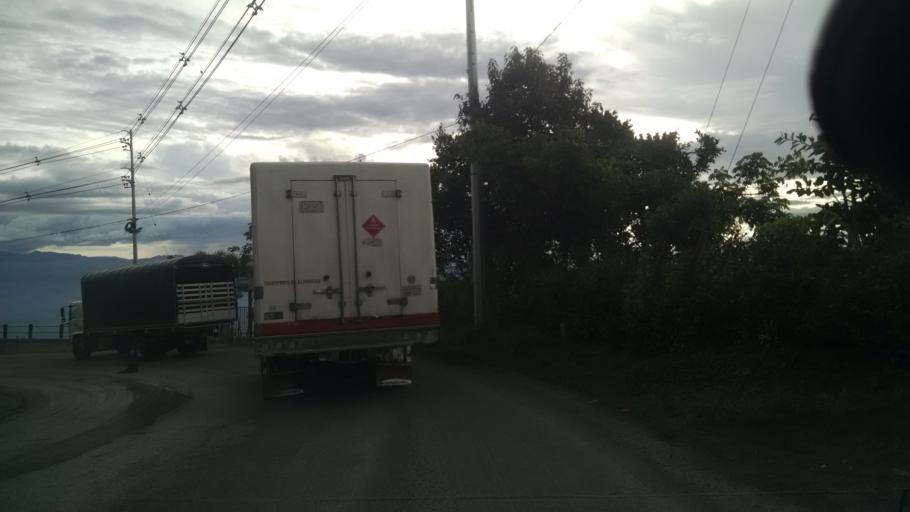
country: CO
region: Antioquia
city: Santa Barbara
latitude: 5.8868
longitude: -75.5728
